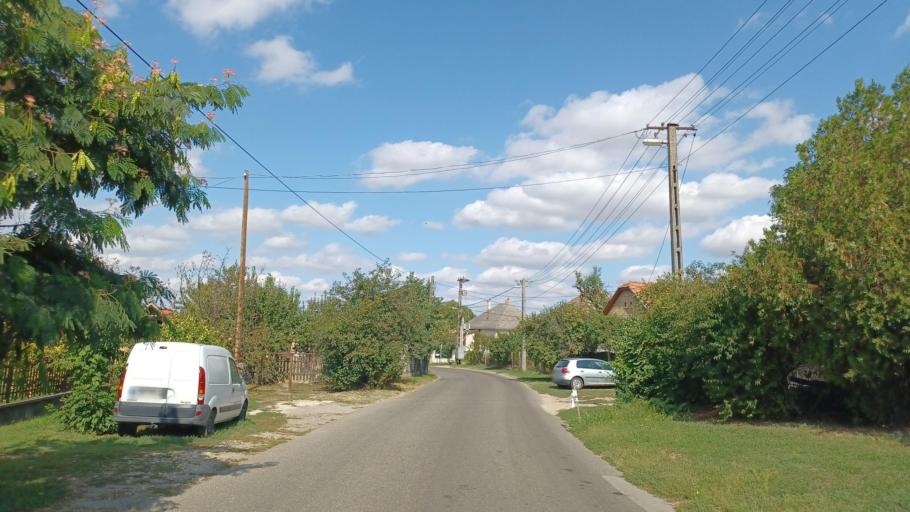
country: HU
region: Tolna
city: Pincehely
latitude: 46.7162
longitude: 18.4758
